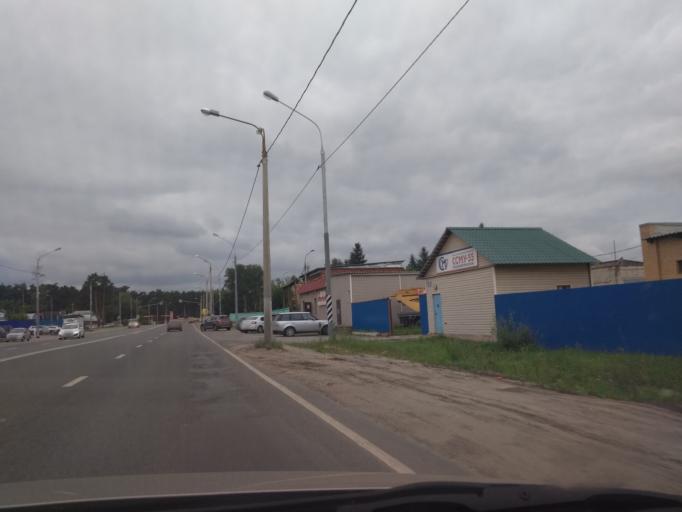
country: RU
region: Moskovskaya
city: Orekhovo-Zuyevo
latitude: 55.8273
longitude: 38.9638
